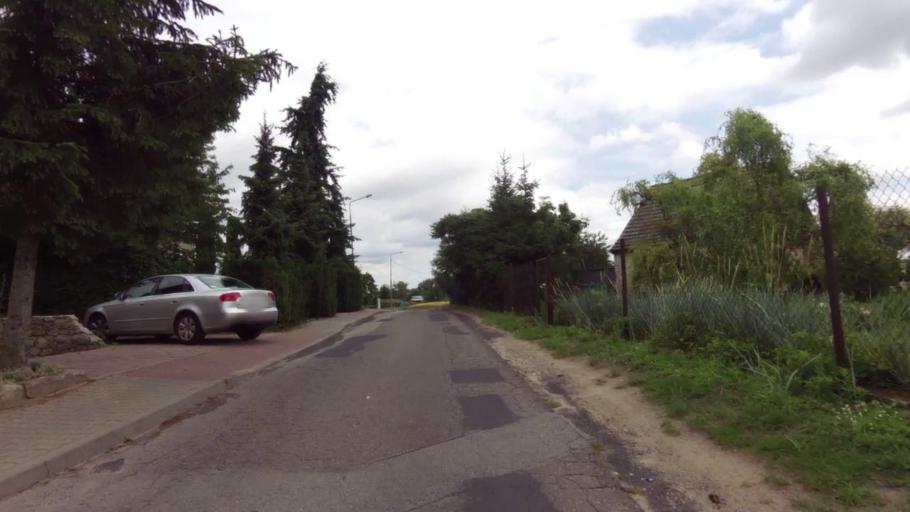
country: PL
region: West Pomeranian Voivodeship
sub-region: Powiat gryfinski
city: Cedynia
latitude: 52.8775
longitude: 14.2132
